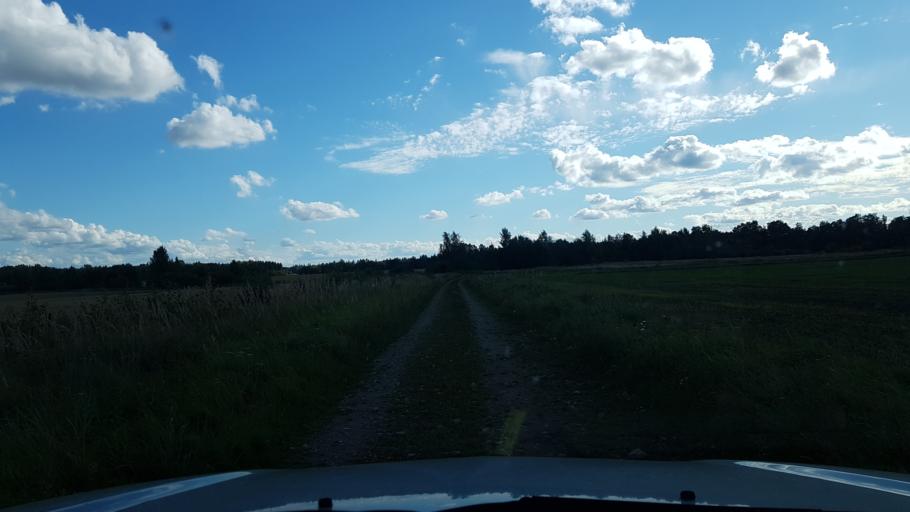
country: EE
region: Harju
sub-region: Rae vald
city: Jueri
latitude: 59.3588
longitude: 24.8553
